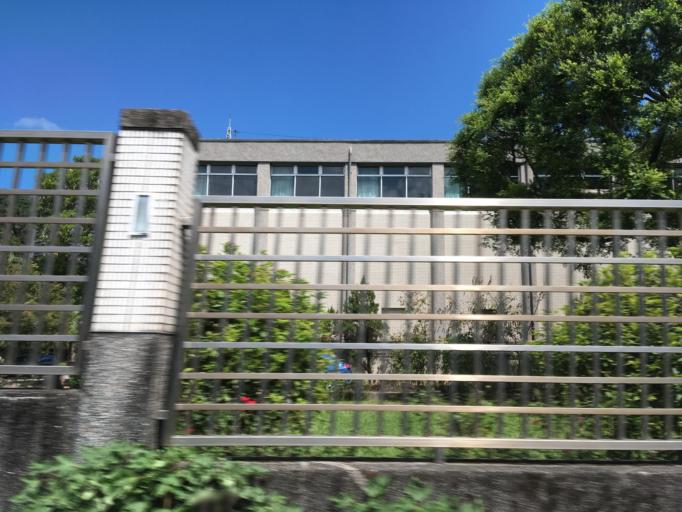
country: TW
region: Taipei
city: Taipei
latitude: 24.9517
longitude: 121.5511
